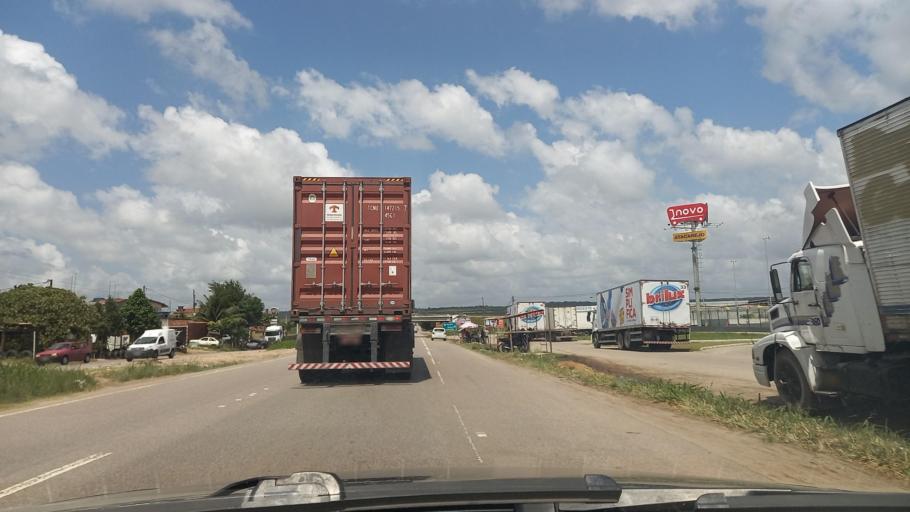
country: BR
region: Pernambuco
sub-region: Goiana
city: Goiana
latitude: -7.5635
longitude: -34.9904
